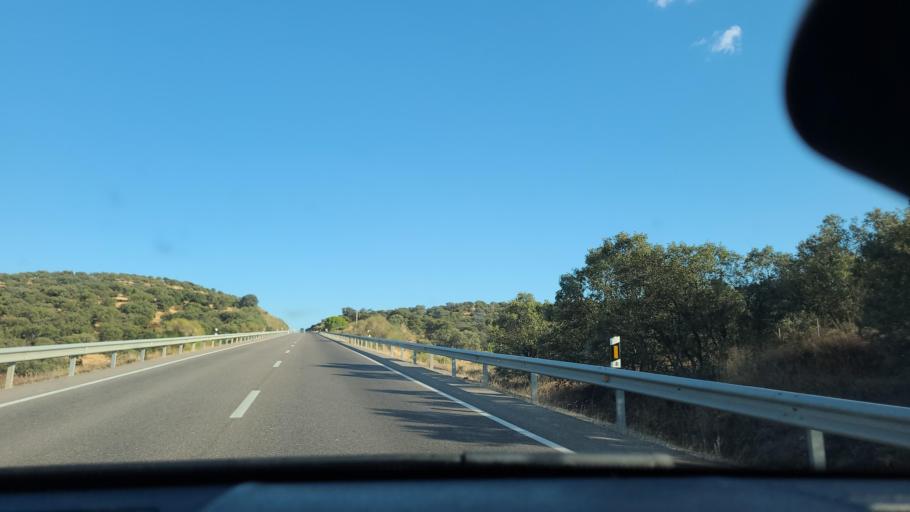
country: ES
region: Andalusia
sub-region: Province of Cordoba
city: Espiel
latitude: 38.1973
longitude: -5.1014
